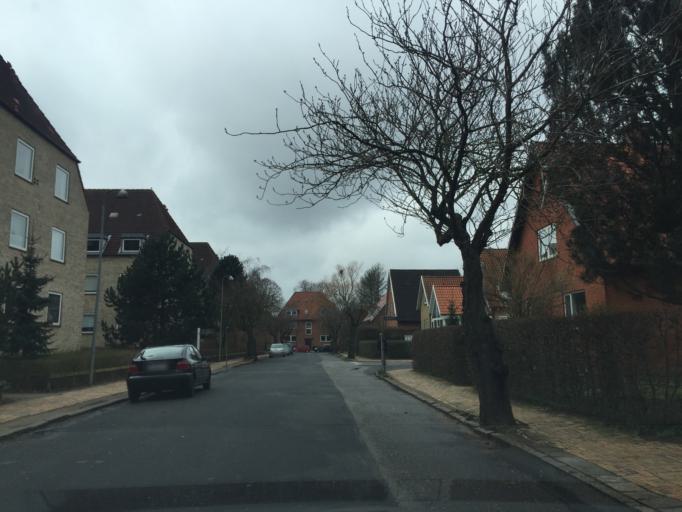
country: DK
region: South Denmark
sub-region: Odense Kommune
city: Odense
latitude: 55.3825
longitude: 10.4023
